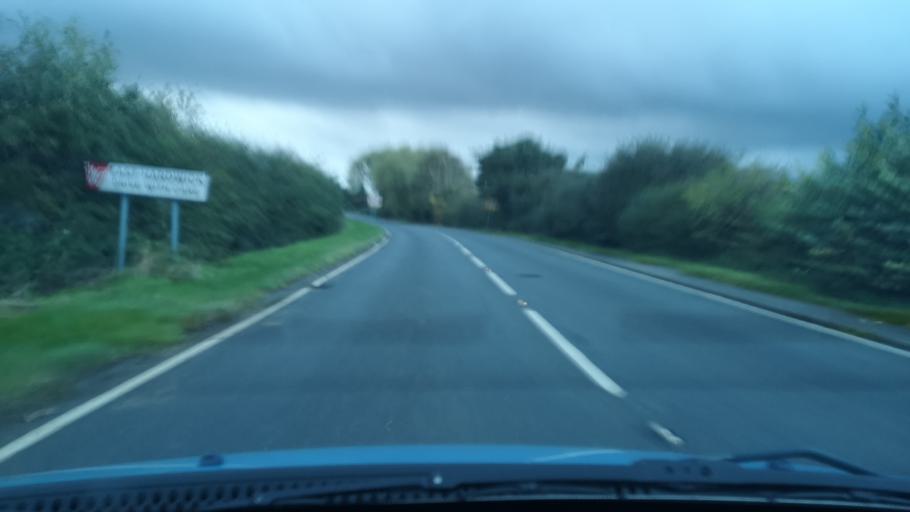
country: GB
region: England
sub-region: City and Borough of Wakefield
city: Badsworth
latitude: 53.6454
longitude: -1.2850
